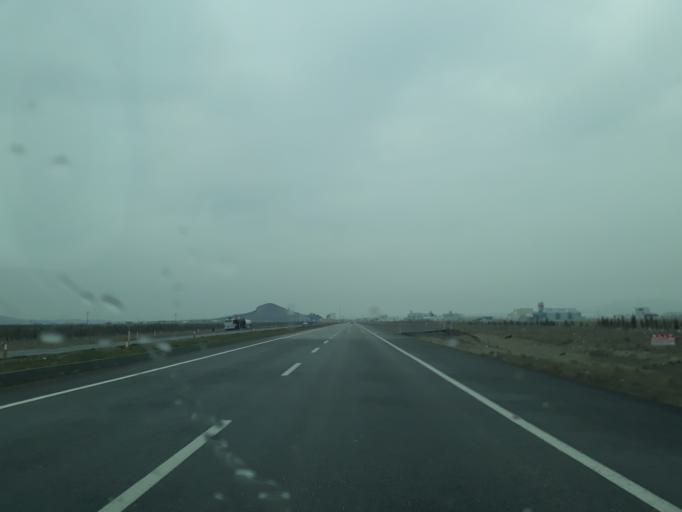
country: TR
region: Konya
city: Karapinar
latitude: 37.7119
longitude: 33.6114
